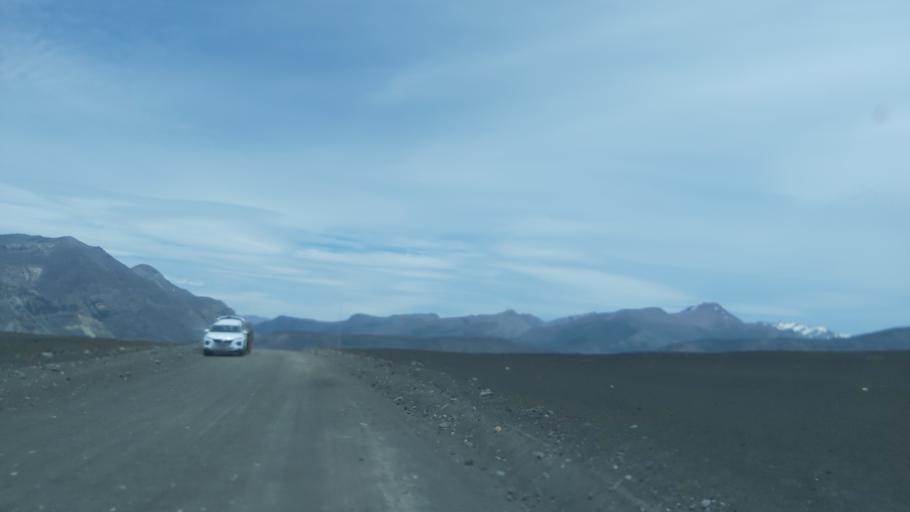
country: AR
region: Neuquen
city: Andacollo
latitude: -37.4363
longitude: -71.2853
